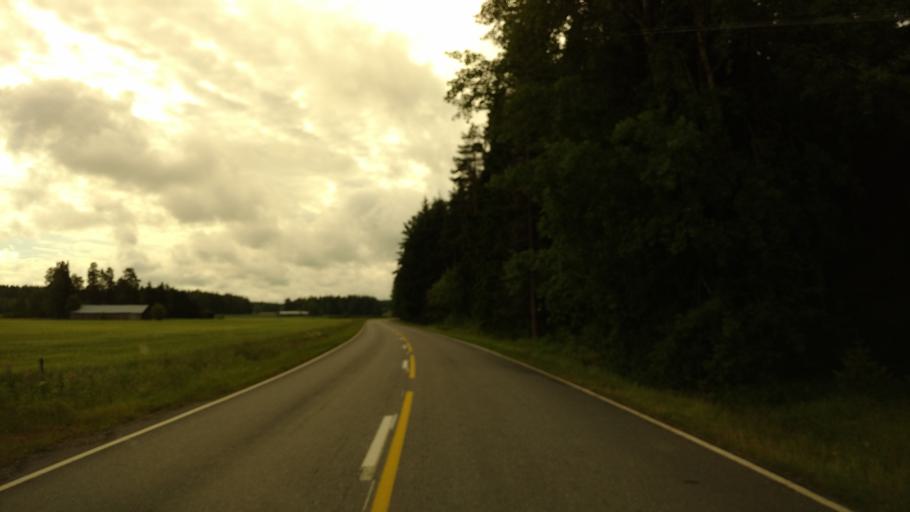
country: FI
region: Varsinais-Suomi
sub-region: Loimaa
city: Koski Tl
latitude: 60.5973
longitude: 23.1279
